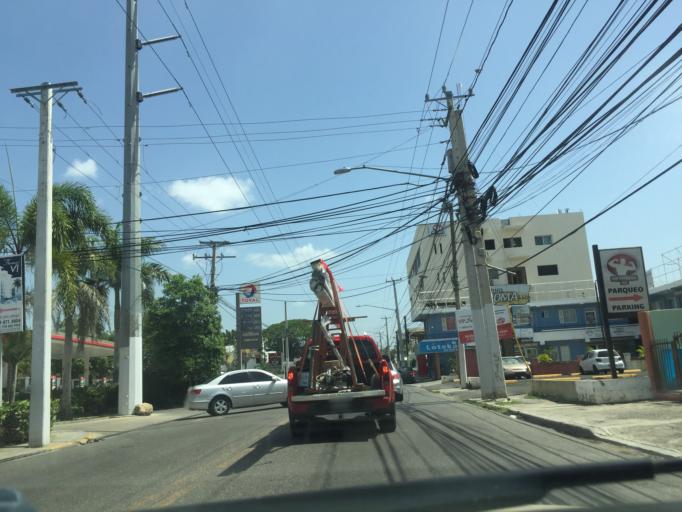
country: DO
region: Santiago
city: Santiago de los Caballeros
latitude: 19.4466
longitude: -70.6671
